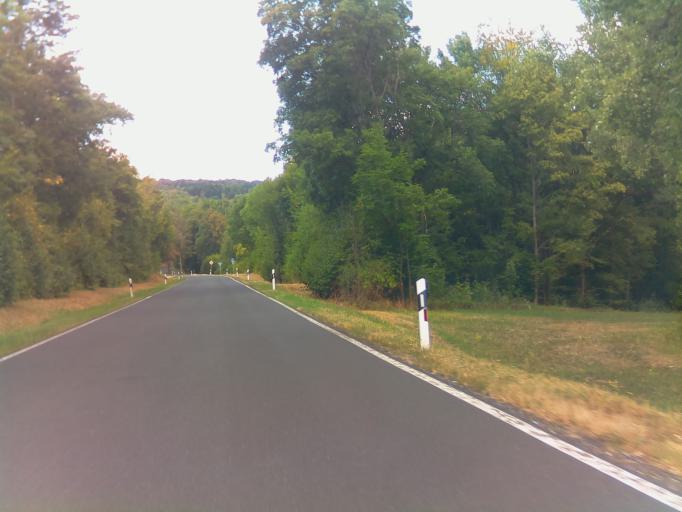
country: DE
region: Bavaria
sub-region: Regierungsbezirk Unterfranken
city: Oberelsbach
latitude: 50.4671
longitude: 10.0994
